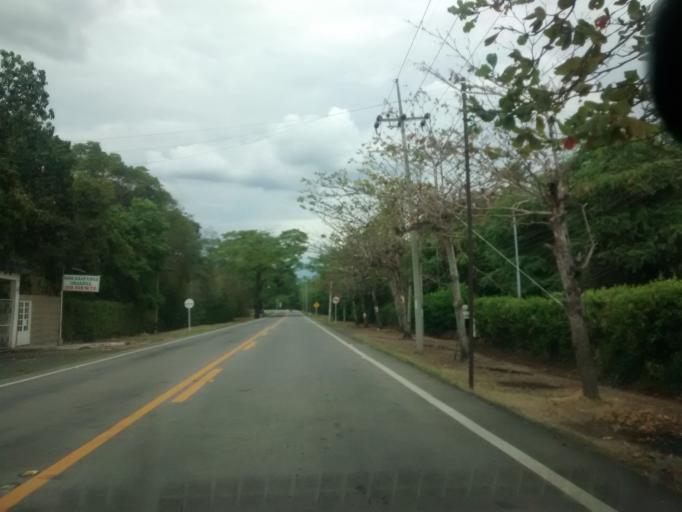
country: CO
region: Cundinamarca
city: Tocaima
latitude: 4.4435
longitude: -74.6713
